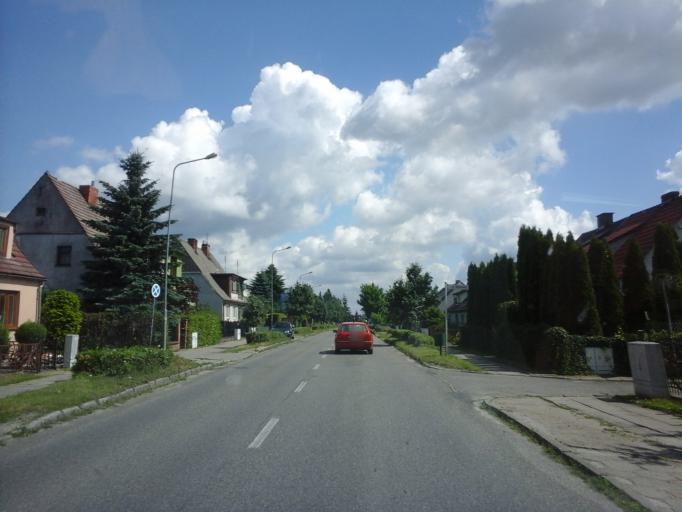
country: PL
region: West Pomeranian Voivodeship
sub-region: Powiat swidwinski
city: Swidwin
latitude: 53.7689
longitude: 15.7595
